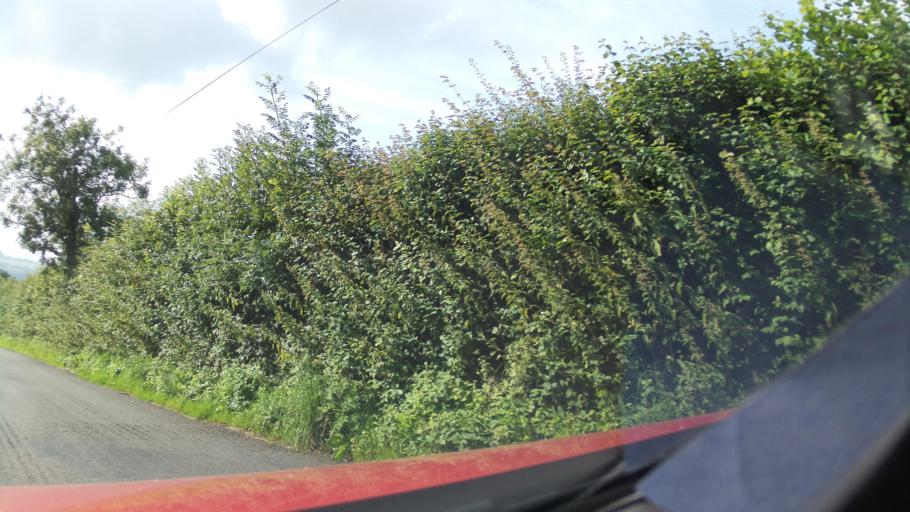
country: GB
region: England
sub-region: Somerset
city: Evercreech
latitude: 51.1627
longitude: -2.5049
